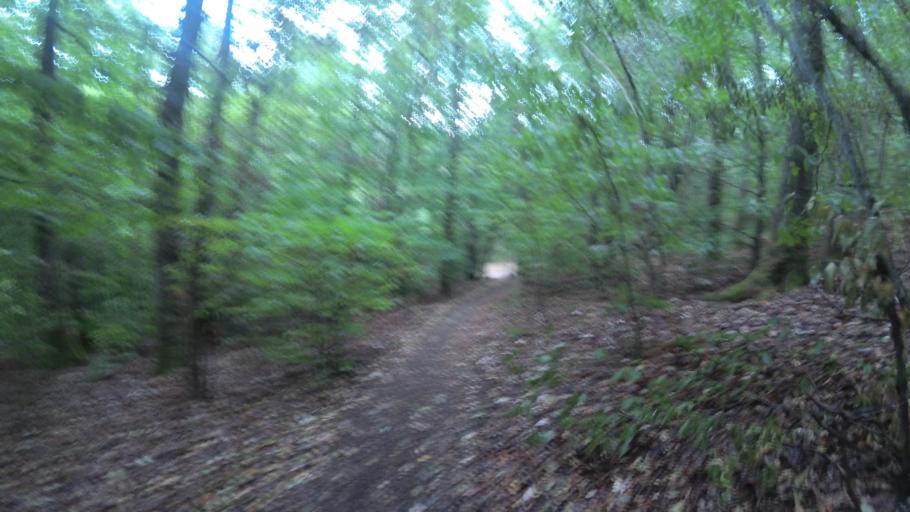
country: DE
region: Rheinland-Pfalz
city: Rorodt
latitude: 49.7669
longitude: 7.0963
